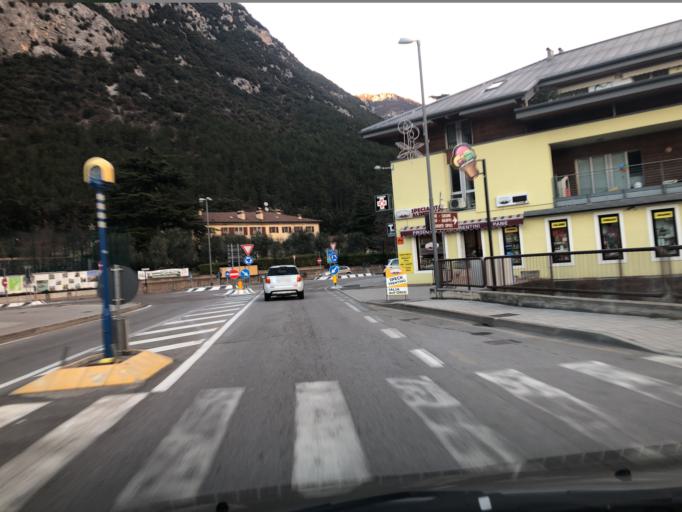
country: IT
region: Trentino-Alto Adige
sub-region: Provincia di Trento
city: Pietramurata
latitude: 46.0466
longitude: 10.9523
